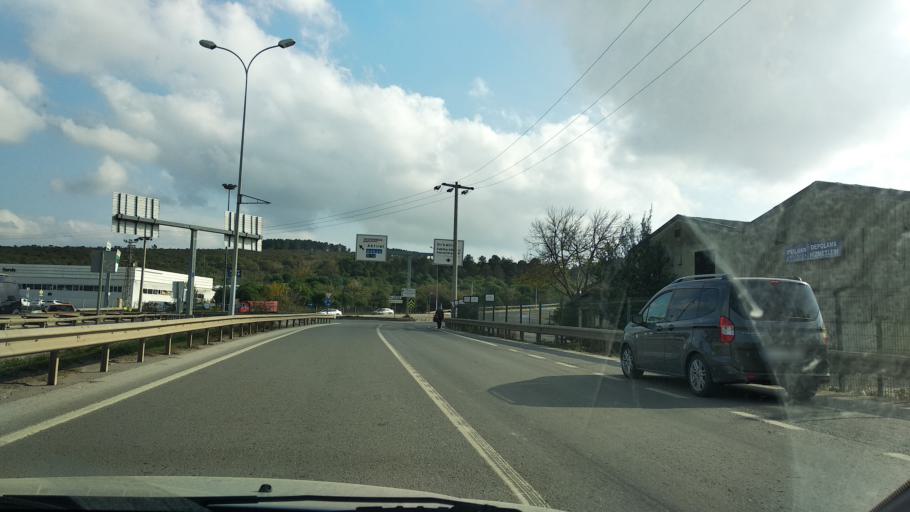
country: TR
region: Istanbul
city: Sultanbeyli
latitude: 40.9310
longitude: 29.3342
